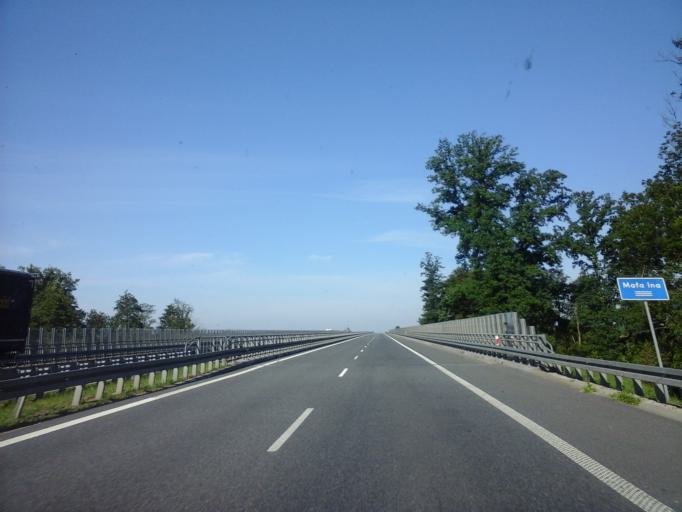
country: PL
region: West Pomeranian Voivodeship
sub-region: Powiat stargardzki
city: Stargard Szczecinski
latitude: 53.3097
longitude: 15.0662
